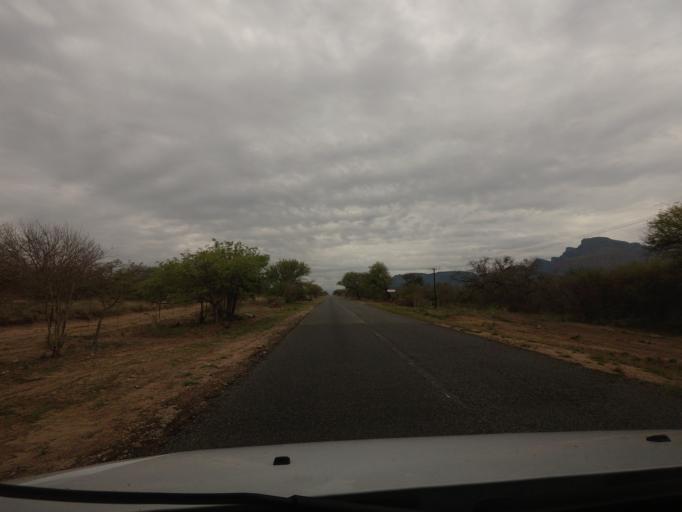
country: ZA
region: Limpopo
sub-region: Mopani District Municipality
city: Hoedspruit
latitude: -24.4741
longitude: 30.8805
